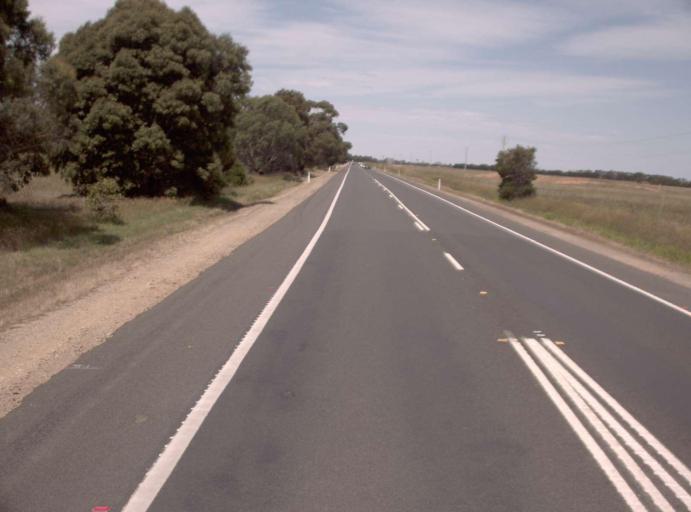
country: AU
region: Victoria
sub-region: Wellington
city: Sale
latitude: -38.1001
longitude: 146.9919
